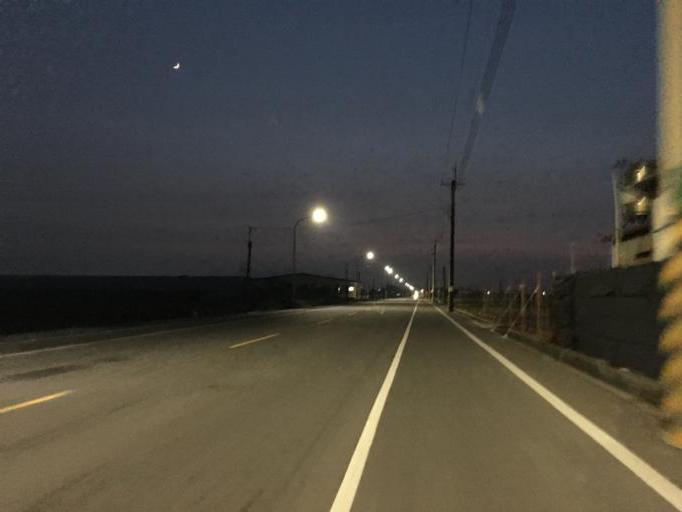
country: TW
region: Taiwan
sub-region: Chiayi
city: Taibao
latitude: 23.5176
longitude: 120.3153
